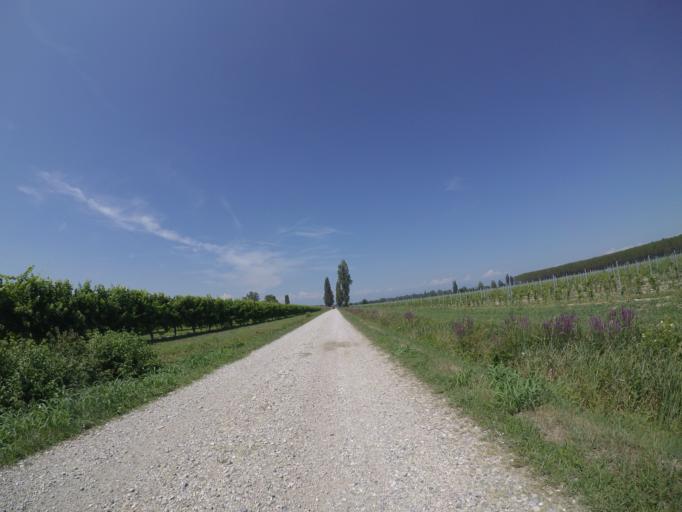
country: IT
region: Friuli Venezia Giulia
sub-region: Provincia di Udine
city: Varmo
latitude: 45.9210
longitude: 13.0032
